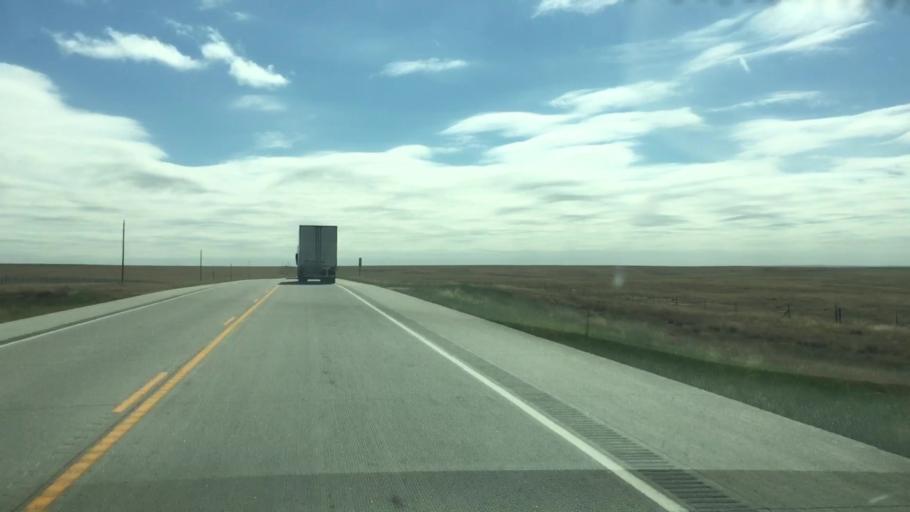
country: US
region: Colorado
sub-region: Lincoln County
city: Hugo
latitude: 39.0188
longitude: -103.3091
